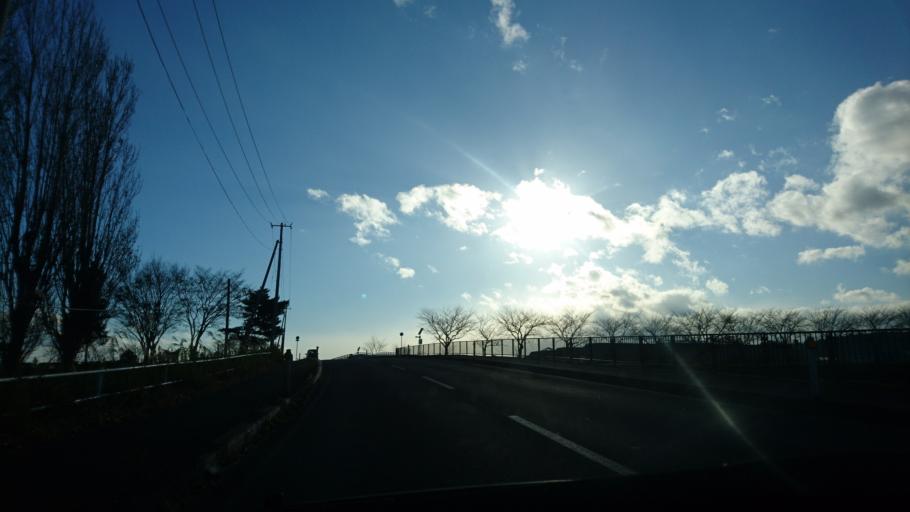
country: JP
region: Iwate
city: Mizusawa
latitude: 39.0568
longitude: 141.1388
